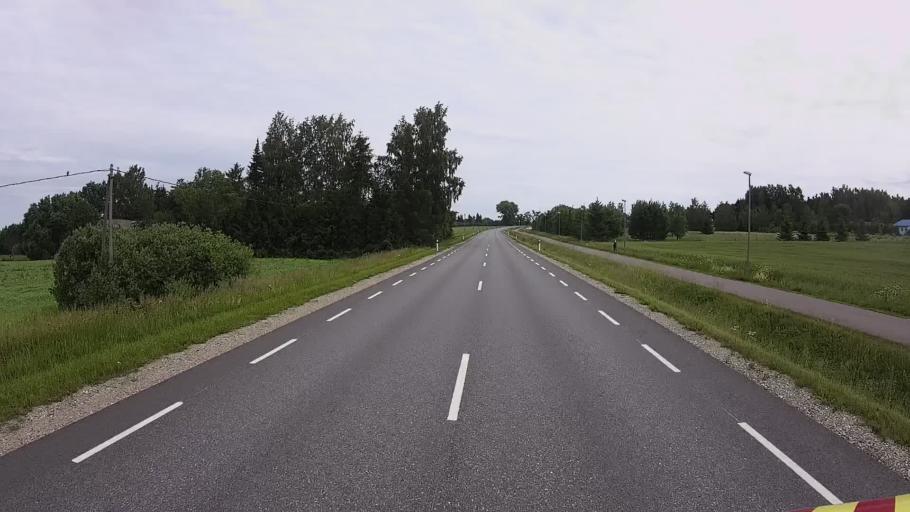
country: EE
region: Viljandimaa
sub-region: Karksi vald
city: Karksi-Nuia
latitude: 58.1131
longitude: 25.5721
